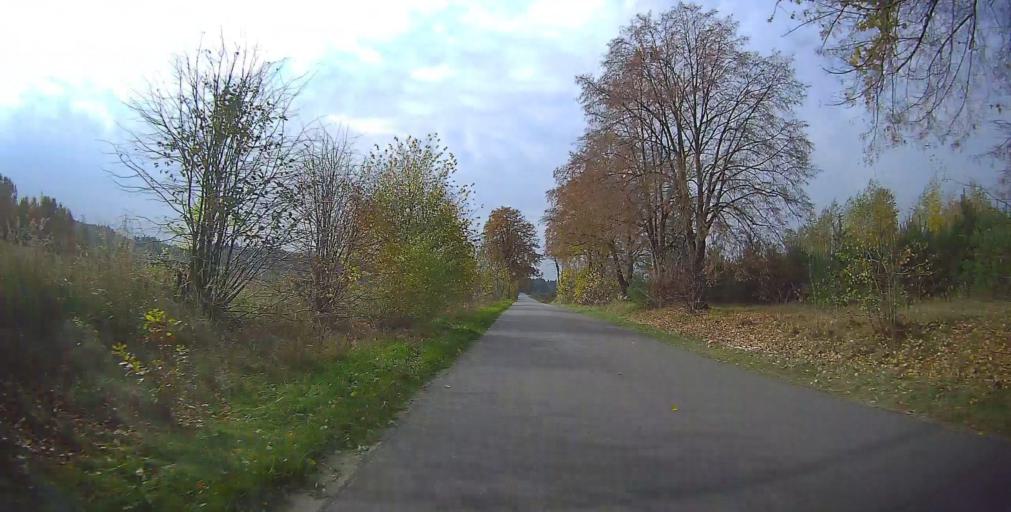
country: PL
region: Masovian Voivodeship
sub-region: Powiat bialobrzeski
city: Wysmierzyce
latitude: 51.6504
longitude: 20.7665
